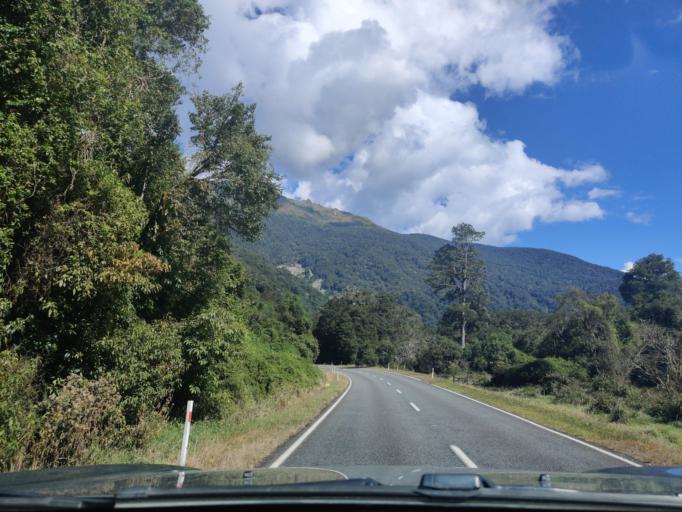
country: NZ
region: Otago
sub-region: Queenstown-Lakes District
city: Wanaka
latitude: -43.9711
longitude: 169.3953
